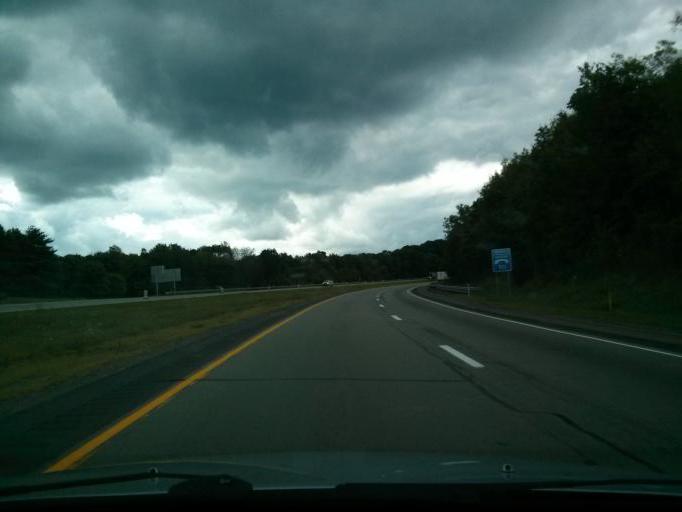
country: US
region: Pennsylvania
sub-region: Clarion County
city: Clarion
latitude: 41.1788
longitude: -79.2482
